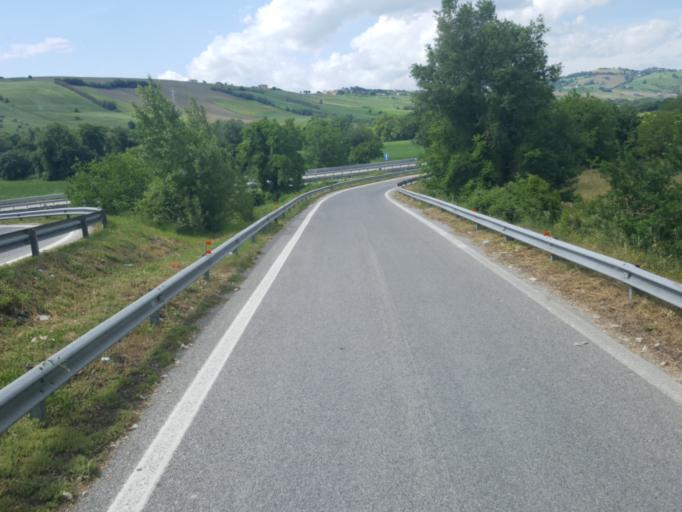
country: IT
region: The Marches
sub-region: Provincia di Macerata
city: Casette Verdini
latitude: 43.2349
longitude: 13.3686
